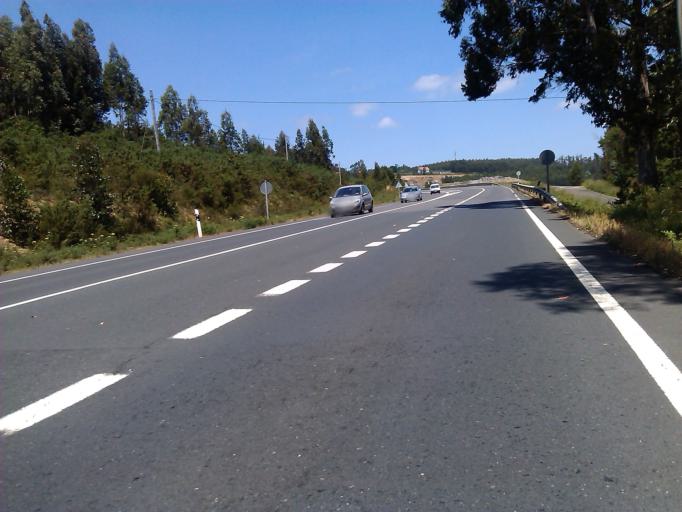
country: ES
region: Galicia
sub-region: Provincia da Coruna
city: Oroso
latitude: 42.9101
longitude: -8.4060
